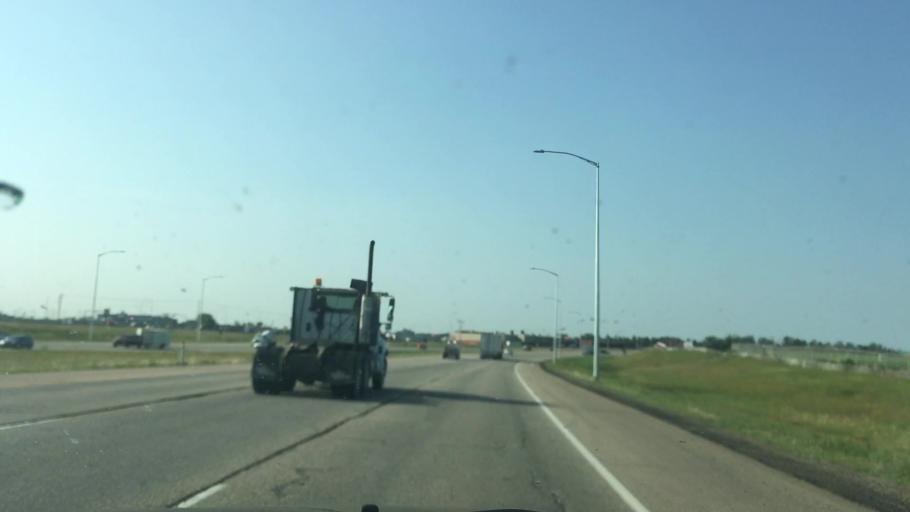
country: CA
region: Alberta
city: Leduc
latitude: 53.2834
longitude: -113.5500
